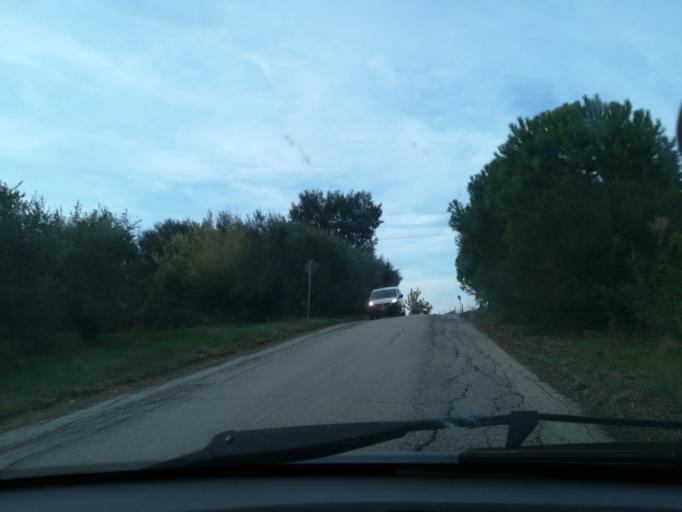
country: IT
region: The Marches
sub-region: Provincia di Macerata
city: Piediripa
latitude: 43.2898
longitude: 13.4885
